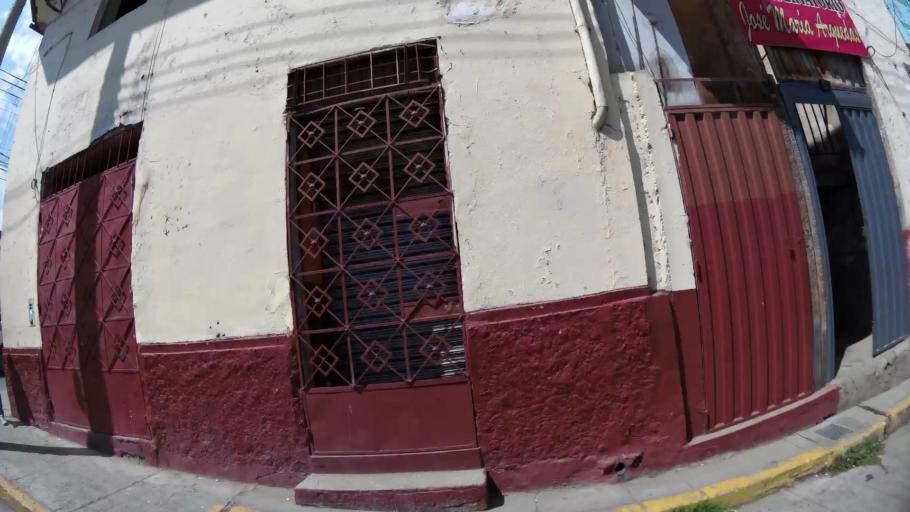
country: PE
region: Junin
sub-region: Provincia de Huancayo
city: Huancayo
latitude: -12.0686
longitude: -75.2073
